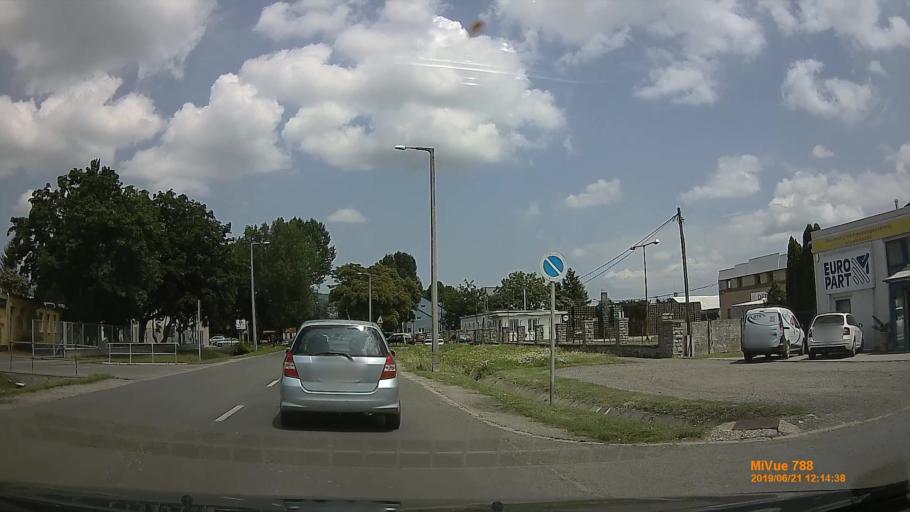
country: HU
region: Baranya
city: Pecs
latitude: 46.0585
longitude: 18.2117
